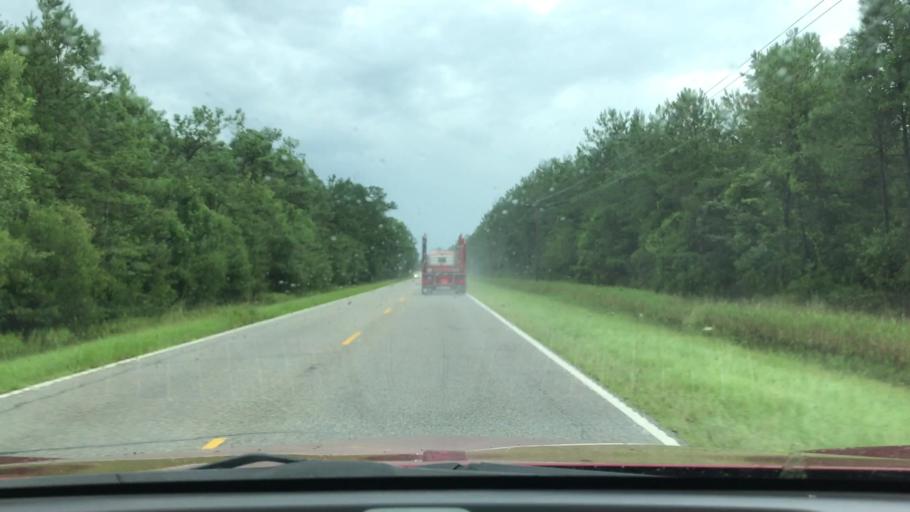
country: US
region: South Carolina
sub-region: Georgetown County
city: Georgetown
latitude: 33.5030
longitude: -79.2569
